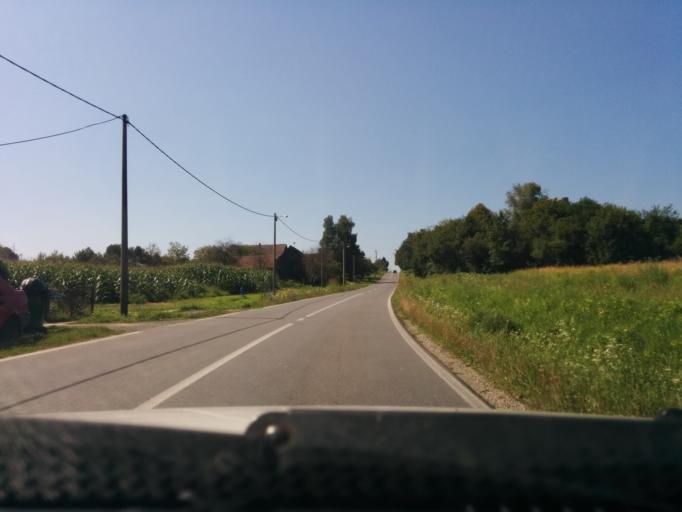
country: HR
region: Sisacko-Moslavacka
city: Lipovljani
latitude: 45.4029
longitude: 16.9053
